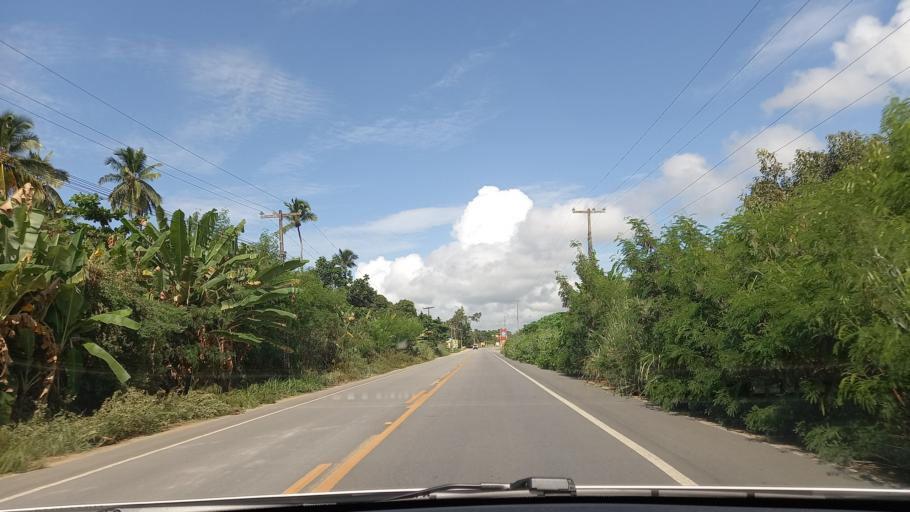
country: BR
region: Alagoas
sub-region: Maragogi
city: Maragogi
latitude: -8.9802
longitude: -35.1881
